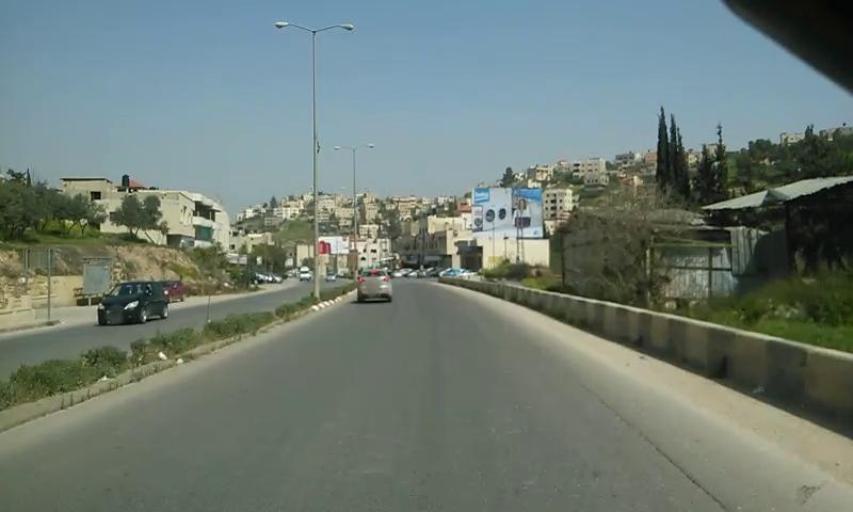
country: PS
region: West Bank
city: Janin
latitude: 32.4451
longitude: 35.2946
